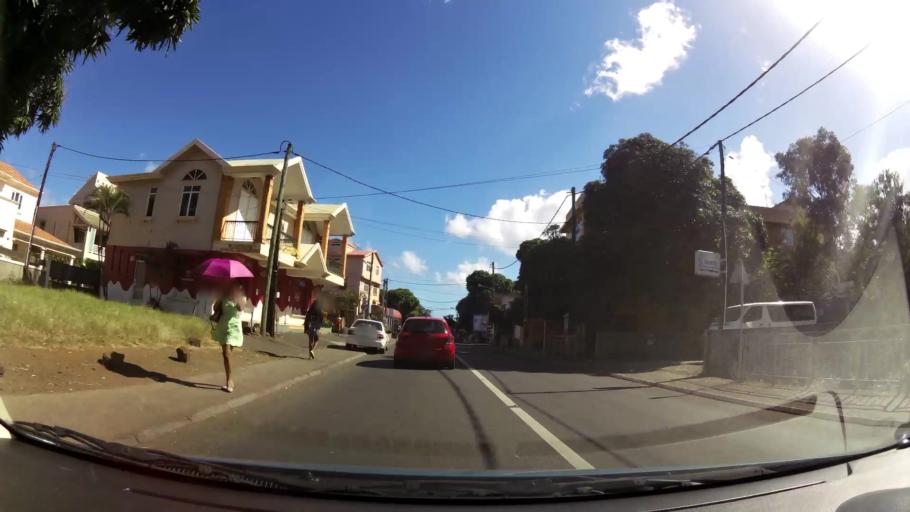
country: MU
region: Black River
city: Cascavelle
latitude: -20.2571
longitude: 57.4173
